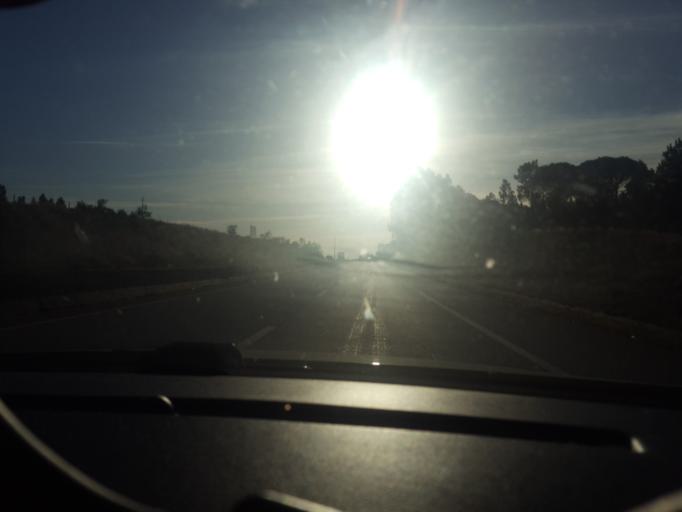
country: PT
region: Viseu
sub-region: Concelho de Carregal do Sal
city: Carregal do Sal
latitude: 40.4623
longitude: -7.9541
